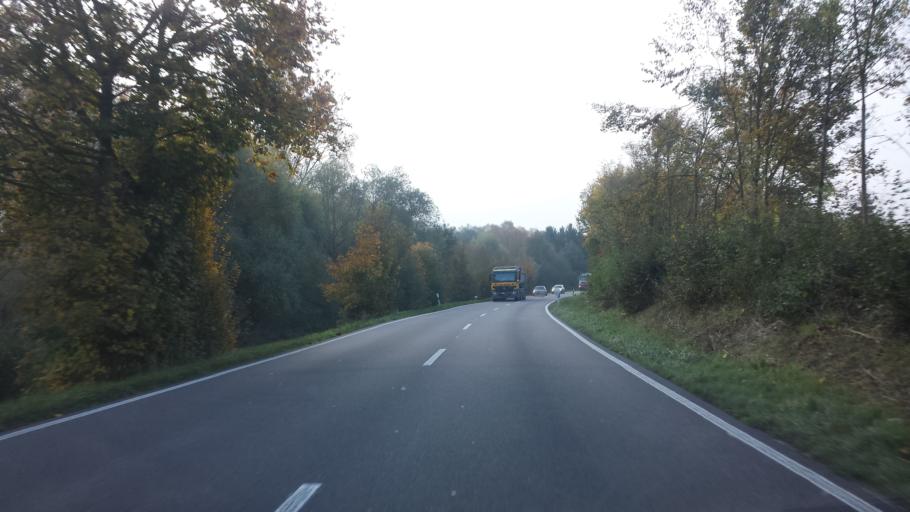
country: DE
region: Baden-Wuerttemberg
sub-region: Karlsruhe Region
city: Ubstadt-Weiher
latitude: 49.1819
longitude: 8.6305
